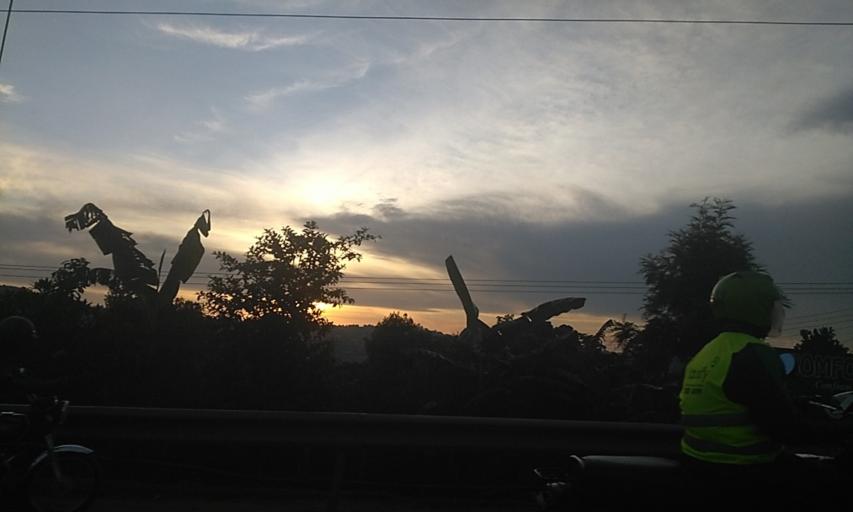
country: UG
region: Central Region
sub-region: Kampala District
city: Kampala
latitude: 0.2713
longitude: 32.5656
